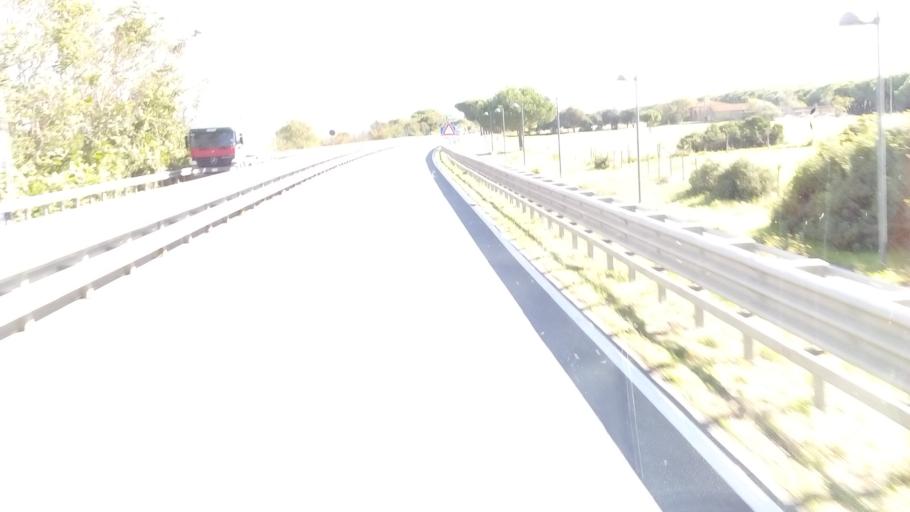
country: IT
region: Tuscany
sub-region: Provincia di Grosseto
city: Fonteblanda
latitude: 42.5450
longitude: 11.1776
